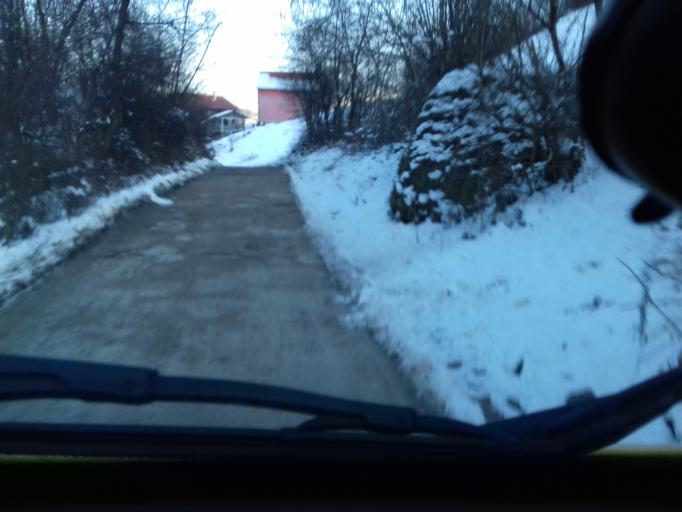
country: BA
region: Federation of Bosnia and Herzegovina
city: Zenica
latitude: 44.1843
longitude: 17.8910
